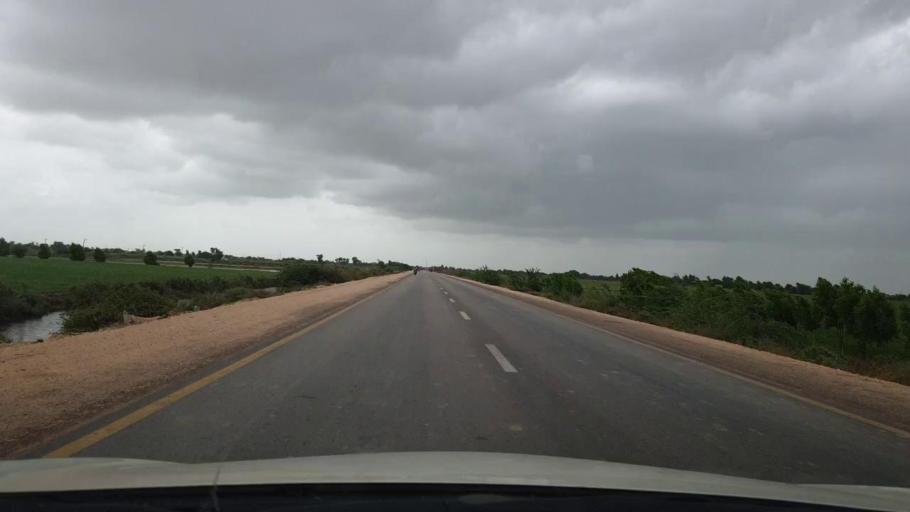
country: PK
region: Sindh
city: Mirpur Batoro
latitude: 24.6432
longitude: 68.4443
